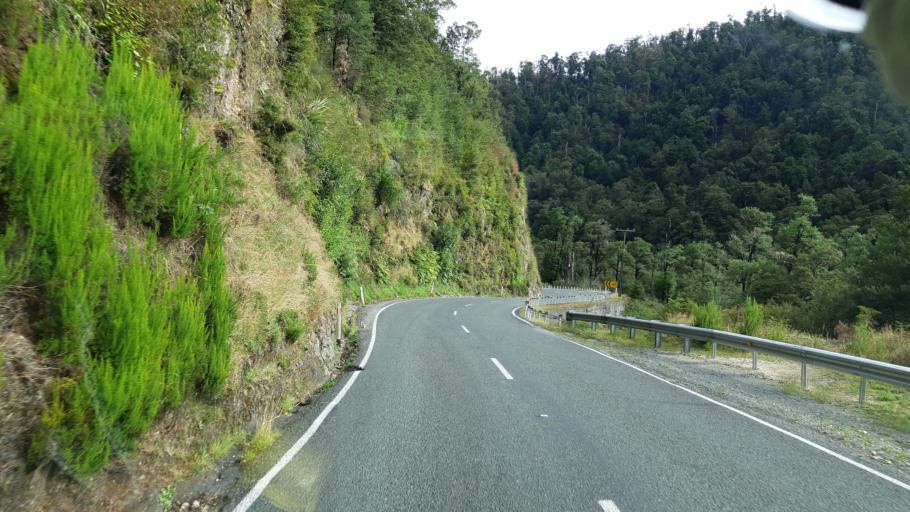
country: NZ
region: West Coast
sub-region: Buller District
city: Westport
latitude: -41.9907
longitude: 172.2189
